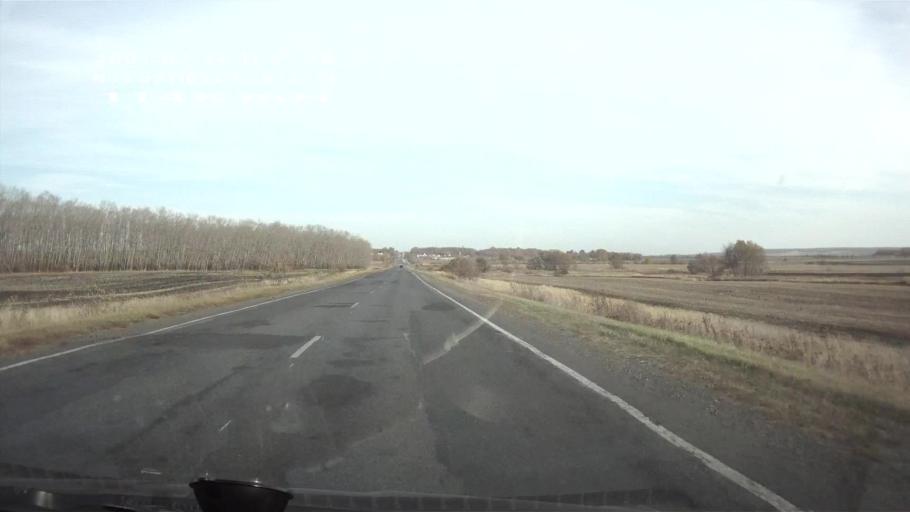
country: RU
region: Mordoviya
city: Atyashevo
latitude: 54.5511
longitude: 45.9570
